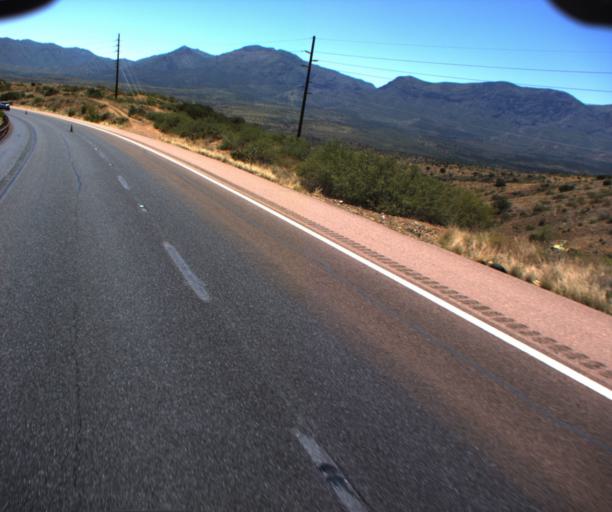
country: US
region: Arizona
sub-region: Gila County
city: Payson
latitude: 34.1520
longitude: -111.3497
